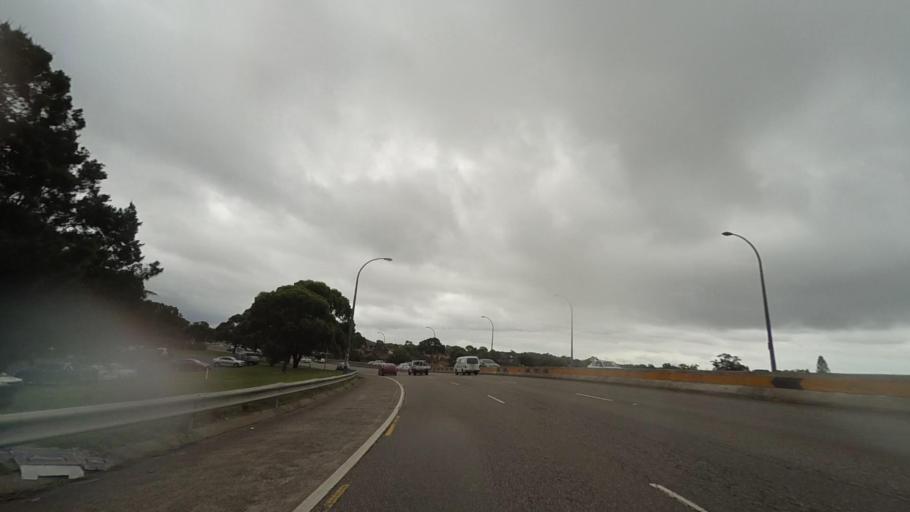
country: AU
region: New South Wales
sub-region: Rockdale
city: Dolls Point
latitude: -34.0051
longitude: 151.1285
